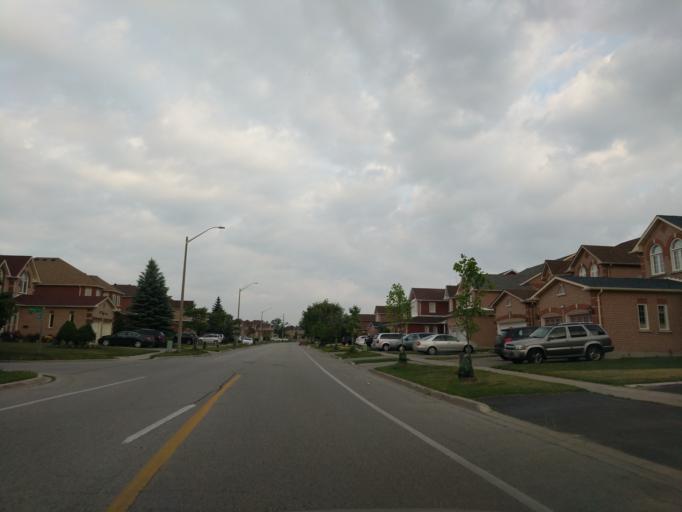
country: CA
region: Ontario
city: Markham
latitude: 43.8470
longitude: -79.2759
